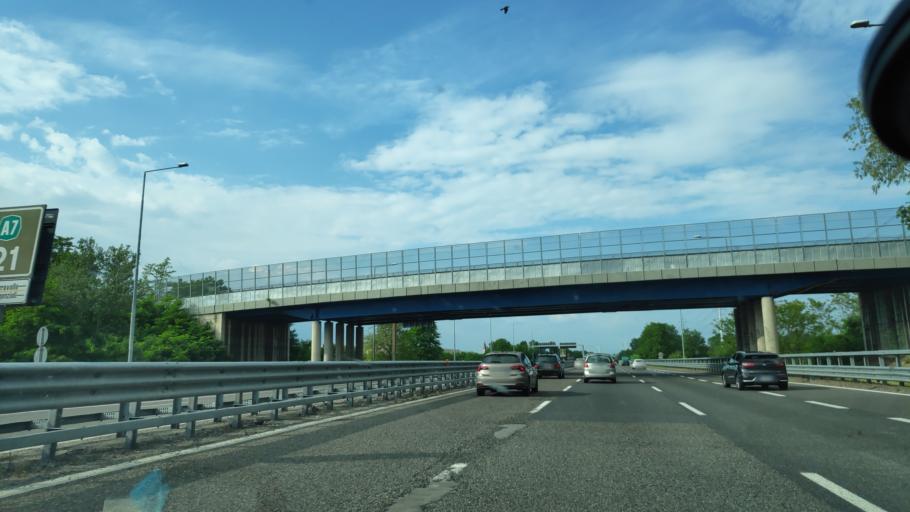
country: IT
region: Lombardy
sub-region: Provincia di Pavia
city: Trivolzio
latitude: 45.2504
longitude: 9.0450
